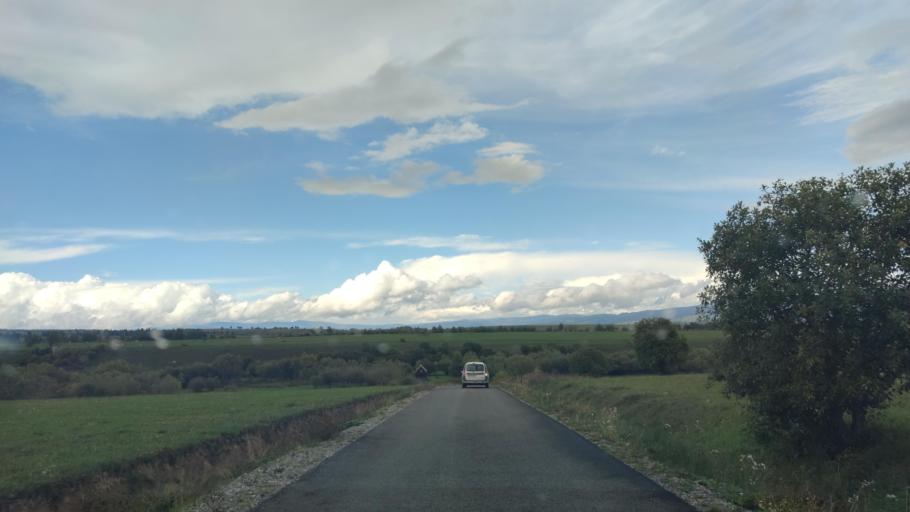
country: RO
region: Harghita
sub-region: Comuna Remetea
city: Remetea
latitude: 46.8118
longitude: 25.3894
